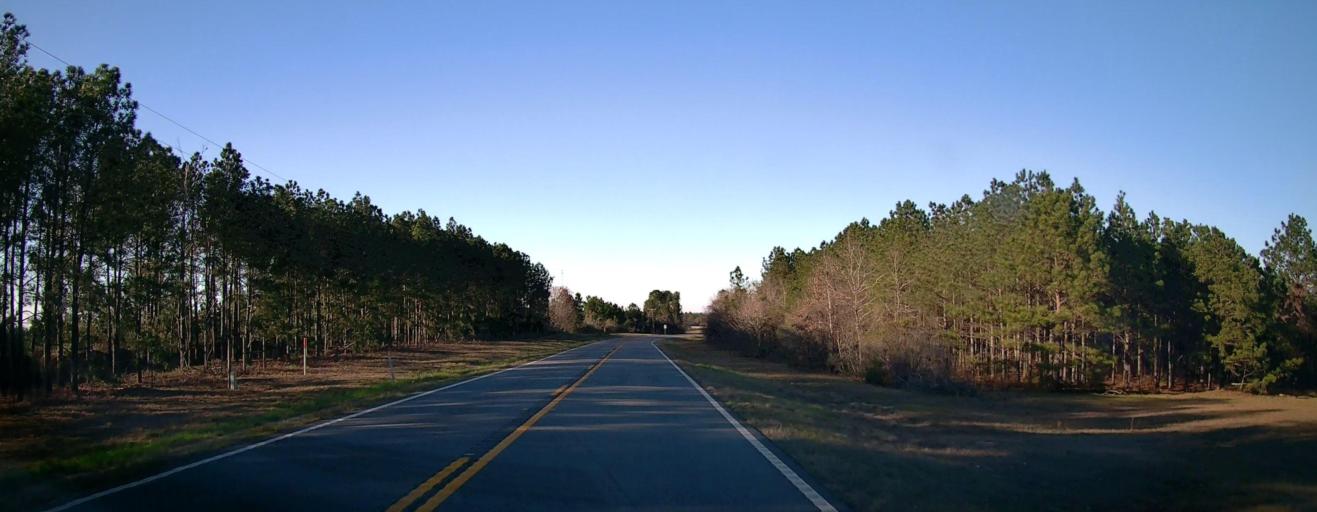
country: US
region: Georgia
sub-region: Talbot County
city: Talbotton
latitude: 32.5561
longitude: -84.4373
